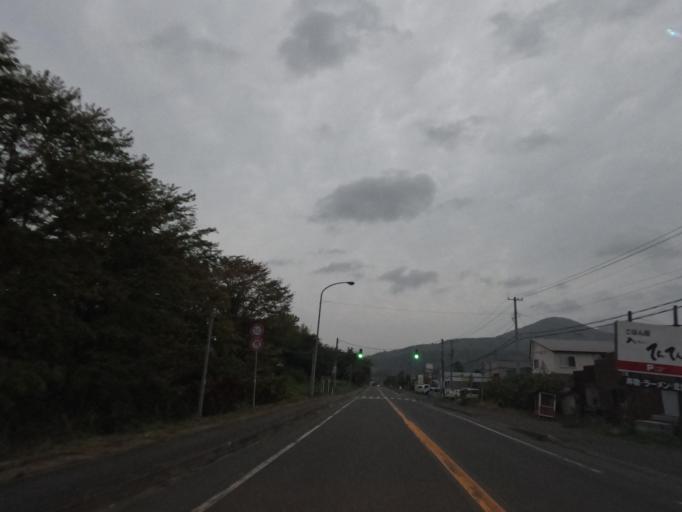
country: JP
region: Hokkaido
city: Date
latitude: 42.5424
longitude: 140.7764
